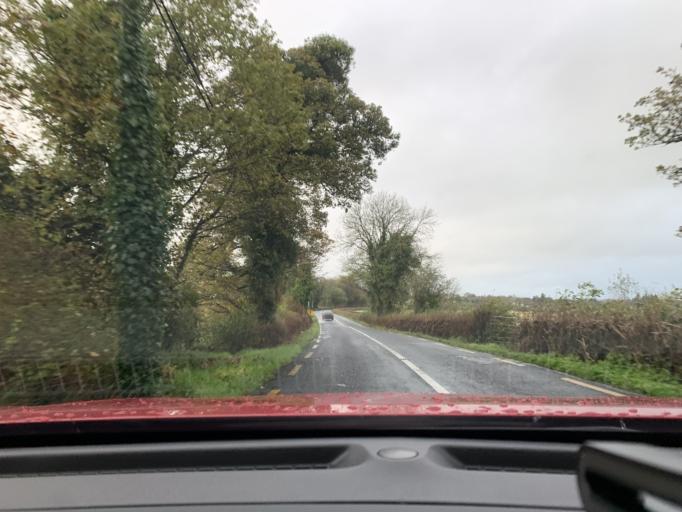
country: IE
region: Connaught
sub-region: Sligo
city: Ballymote
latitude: 54.0463
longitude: -8.5232
